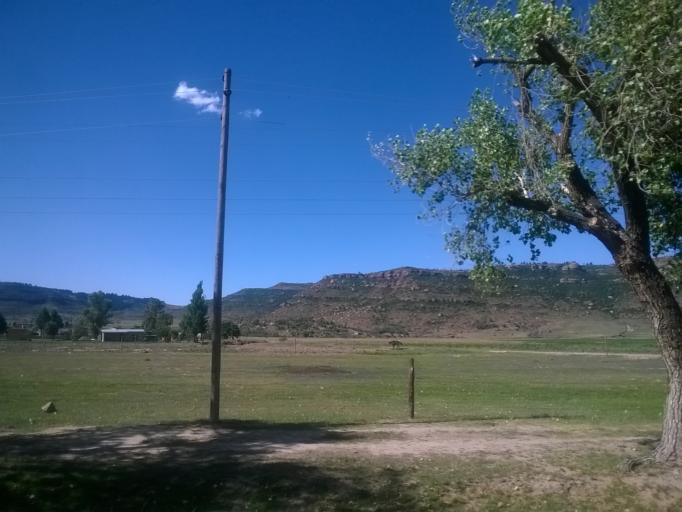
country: LS
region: Maseru
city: Maseru
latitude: -29.2673
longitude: 27.5770
